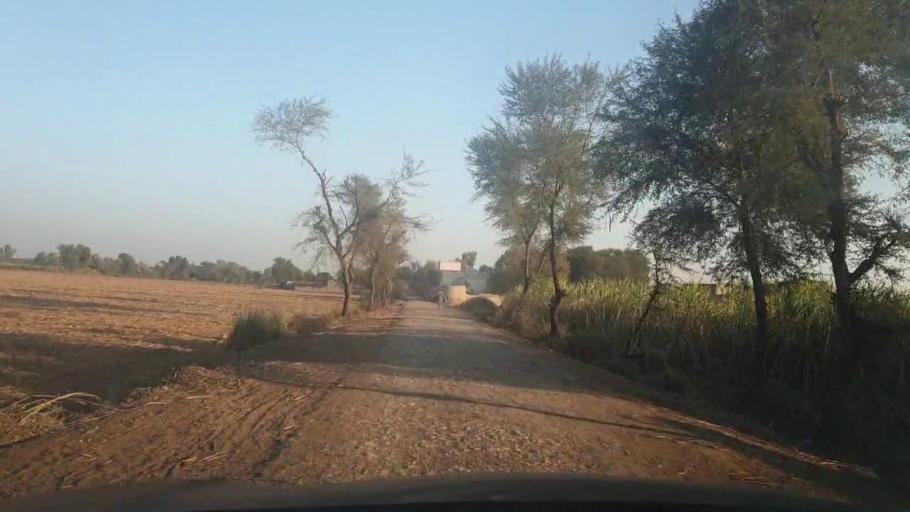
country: PK
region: Sindh
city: Mirpur Mathelo
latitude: 28.1735
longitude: 69.5743
